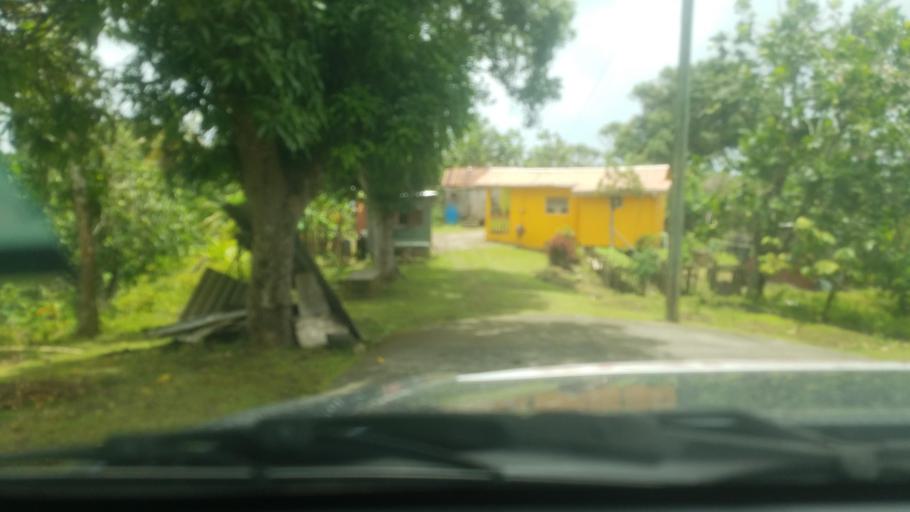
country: LC
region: Laborie Quarter
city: Laborie
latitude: 13.7756
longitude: -60.9956
